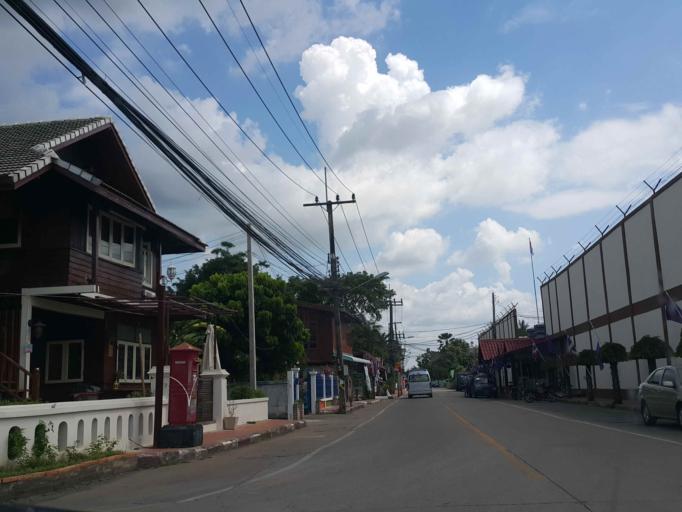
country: TH
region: Nan
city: Nan
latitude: 18.7724
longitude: 100.7721
